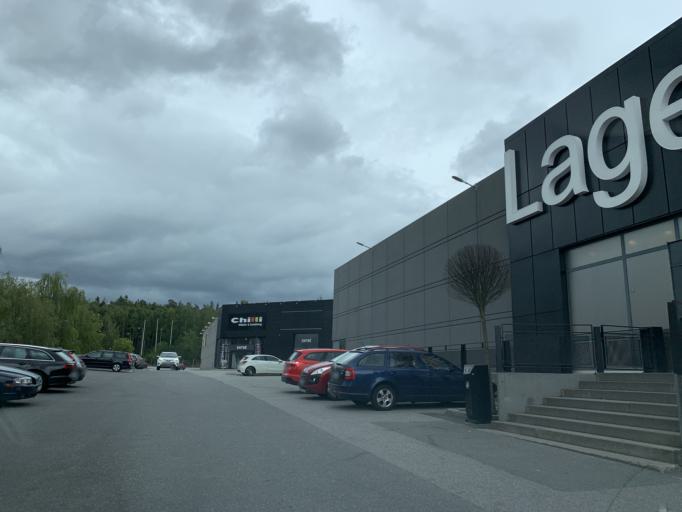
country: SE
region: Stockholm
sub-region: Huddinge Kommun
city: Segeltorp
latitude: 59.2664
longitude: 17.9214
